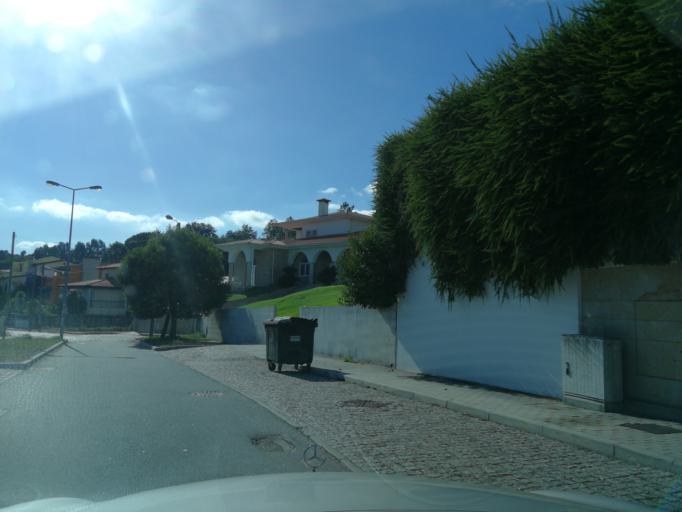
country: PT
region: Braga
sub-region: Braga
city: Adaufe
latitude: 41.5735
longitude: -8.3788
